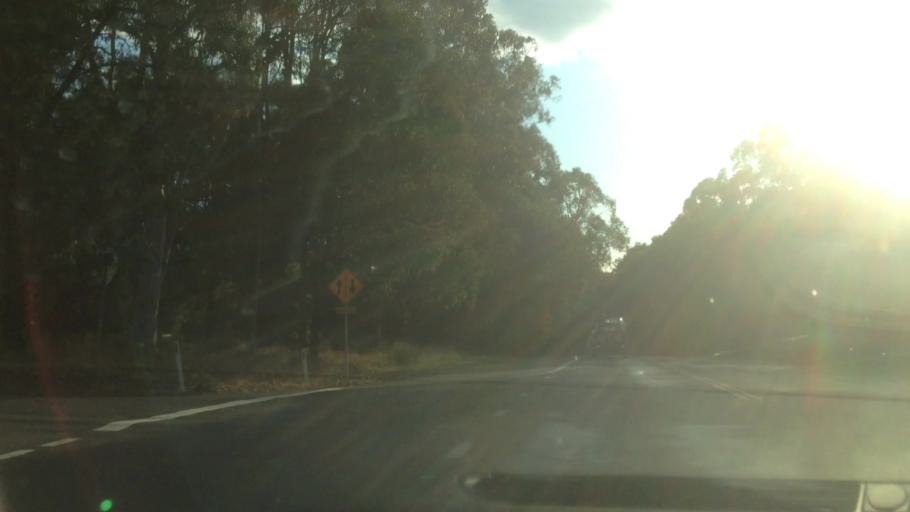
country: AU
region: New South Wales
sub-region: Cessnock
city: Heddon Greta
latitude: -32.8301
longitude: 151.5133
